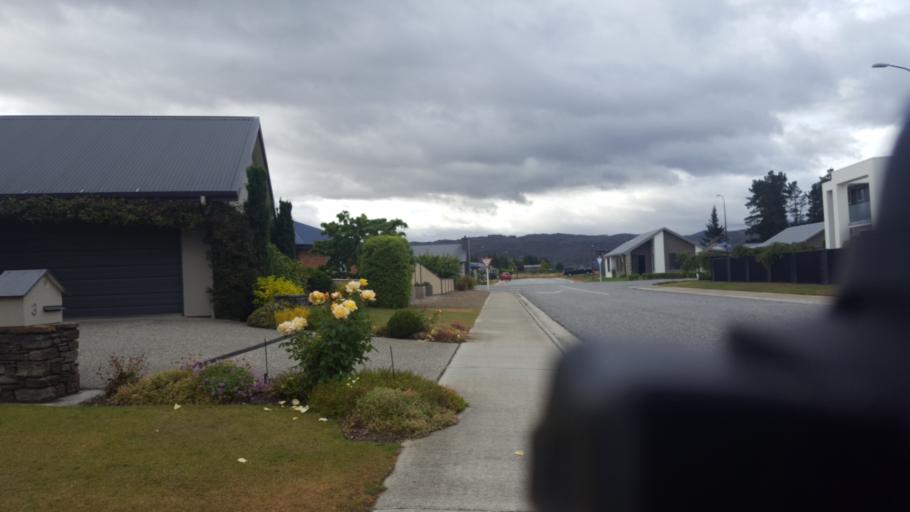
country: NZ
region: Otago
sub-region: Queenstown-Lakes District
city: Wanaka
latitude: -45.2408
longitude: 169.3775
